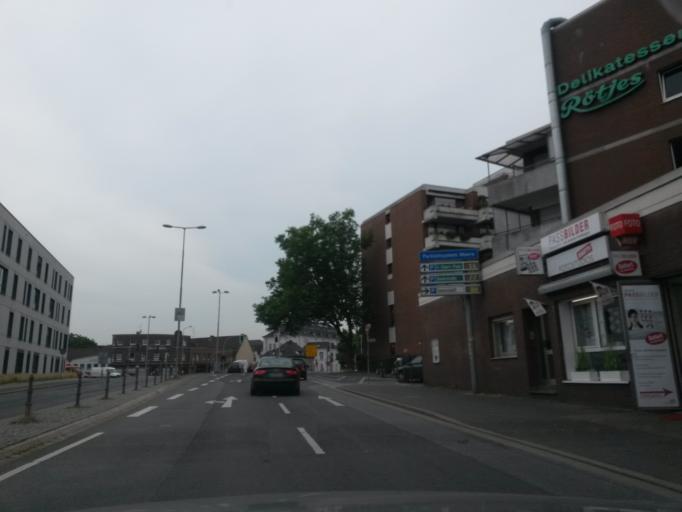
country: DE
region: North Rhine-Westphalia
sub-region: Regierungsbezirk Dusseldorf
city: Moers
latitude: 51.4530
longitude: 6.6264
